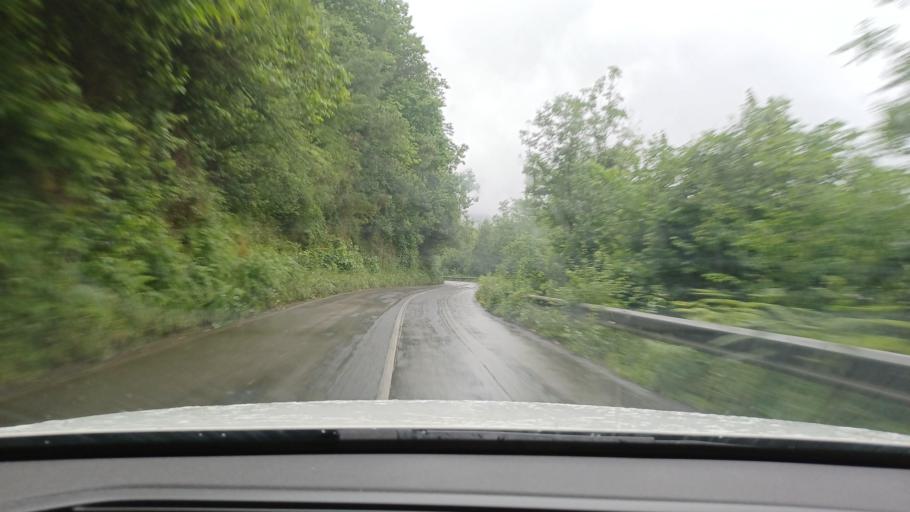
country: ES
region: Asturias
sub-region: Province of Asturias
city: Castandiello
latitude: 43.3089
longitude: -5.8972
